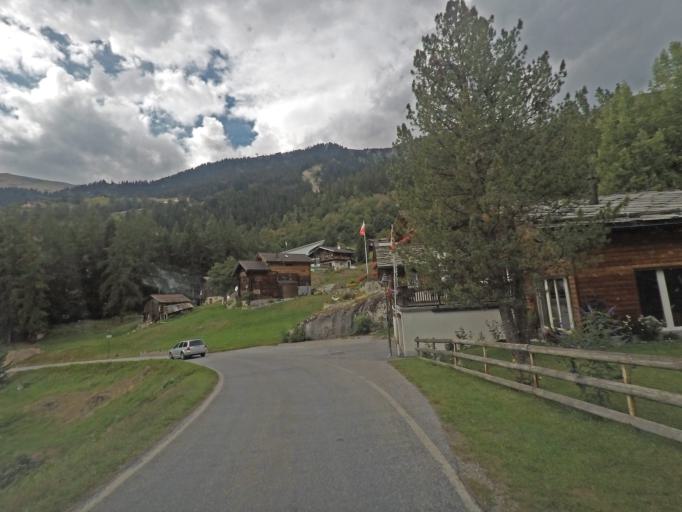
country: CH
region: Valais
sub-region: Brig District
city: Naters
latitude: 46.3654
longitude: 7.9909
